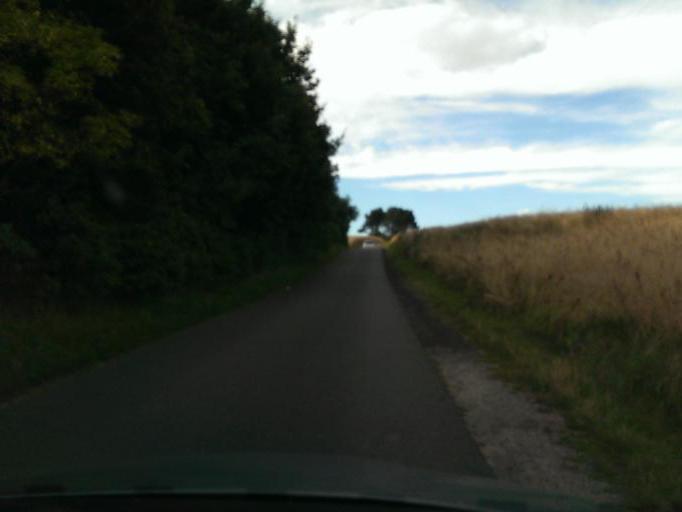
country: DK
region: Central Jutland
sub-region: Syddjurs Kommune
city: Ronde
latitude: 56.1088
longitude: 10.5057
